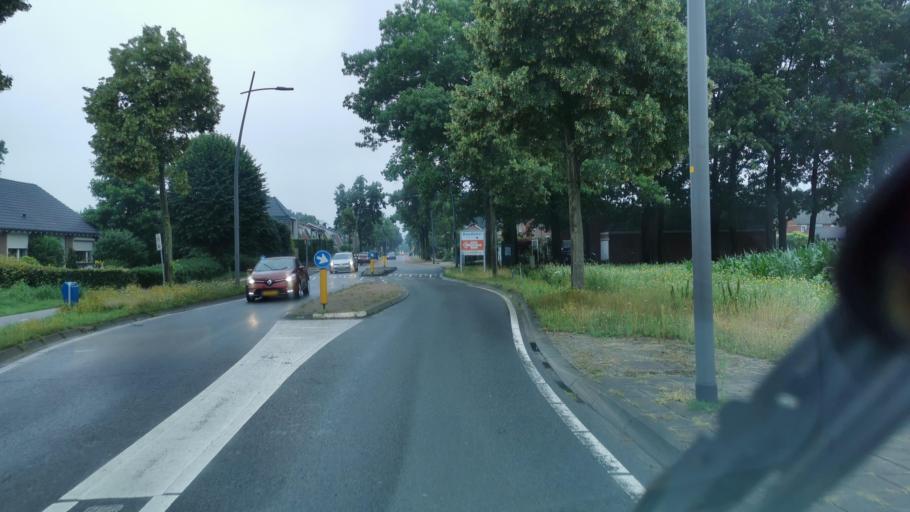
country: NL
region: Overijssel
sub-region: Gemeente Losser
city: Losser
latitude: 52.2438
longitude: 7.0299
